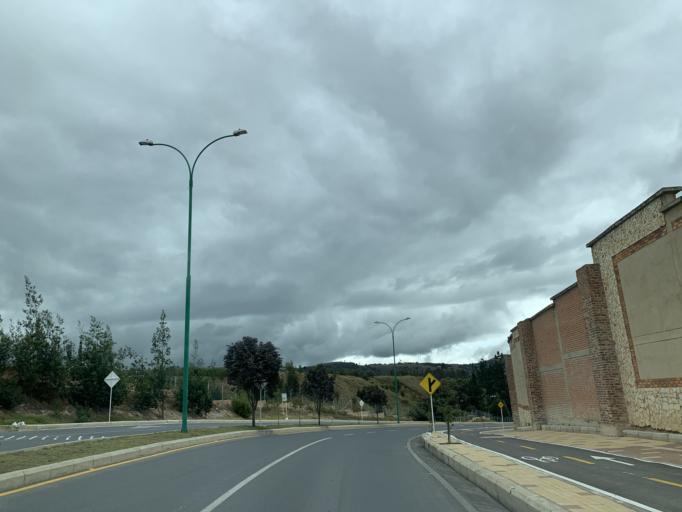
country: CO
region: Boyaca
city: Tunja
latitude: 5.5396
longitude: -73.3476
